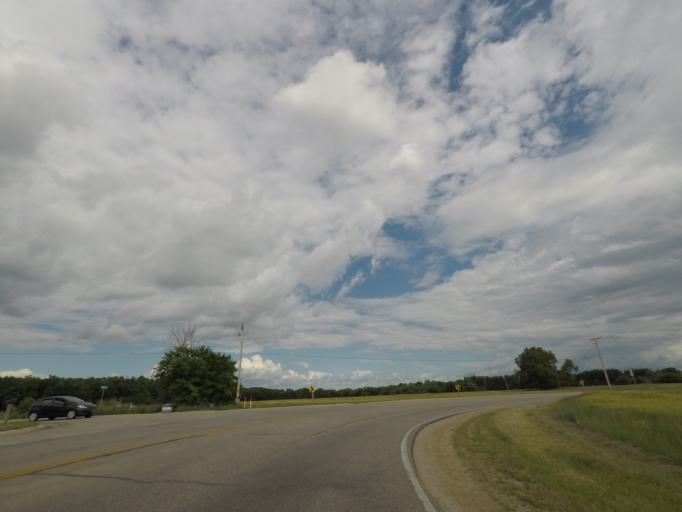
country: US
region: Wisconsin
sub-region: Dane County
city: Belleville
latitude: 42.8567
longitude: -89.5239
